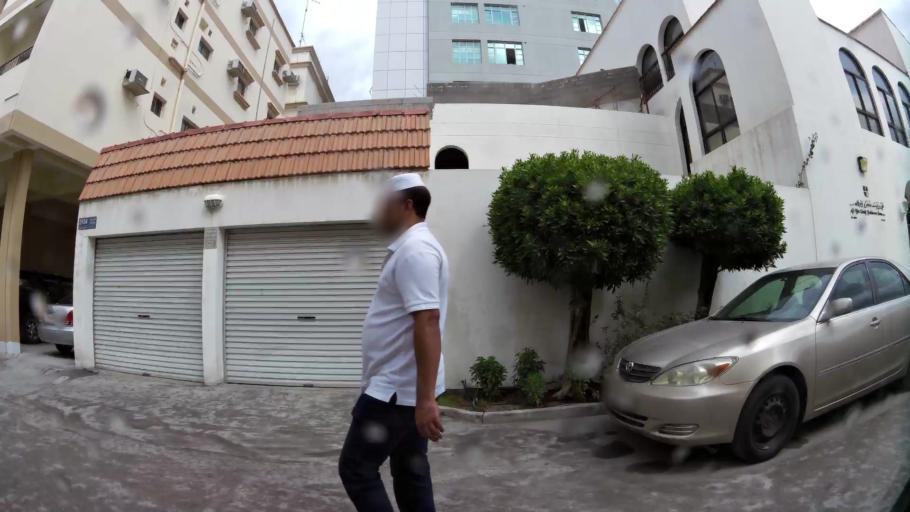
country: BH
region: Manama
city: Manama
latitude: 26.2255
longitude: 50.5952
